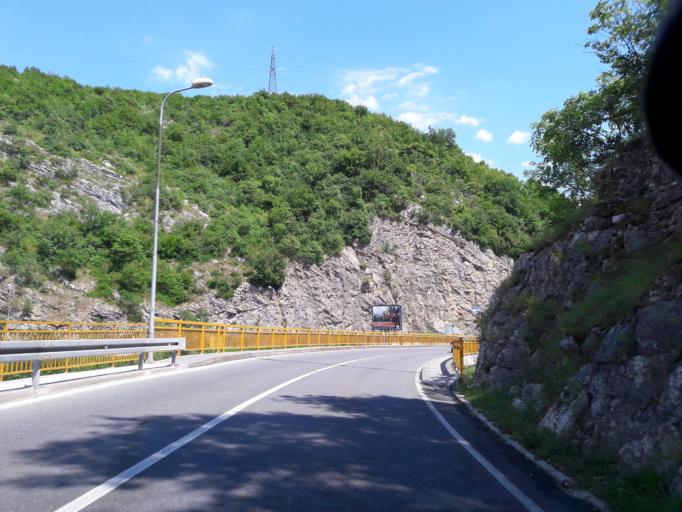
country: BA
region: Republika Srpska
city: Mrkonjic Grad
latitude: 44.4153
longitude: 17.0927
